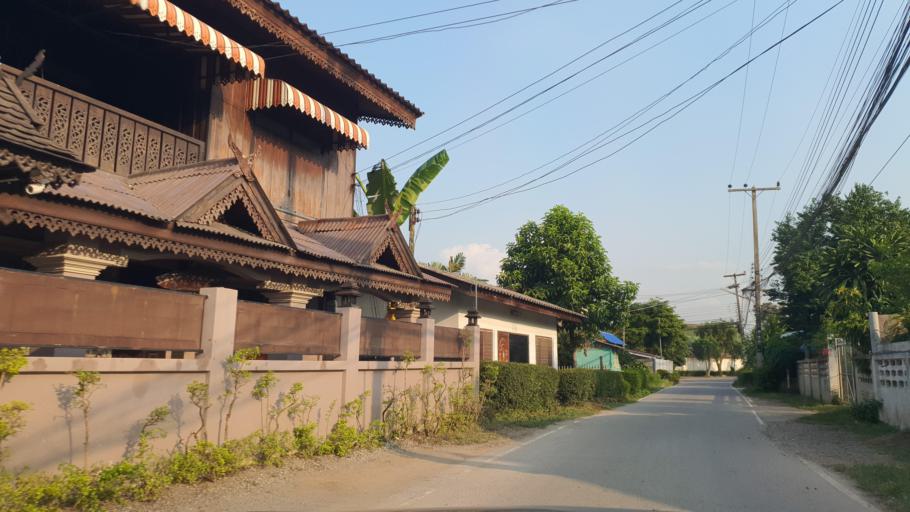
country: TH
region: Chiang Mai
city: San Pa Tong
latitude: 18.6370
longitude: 98.8623
